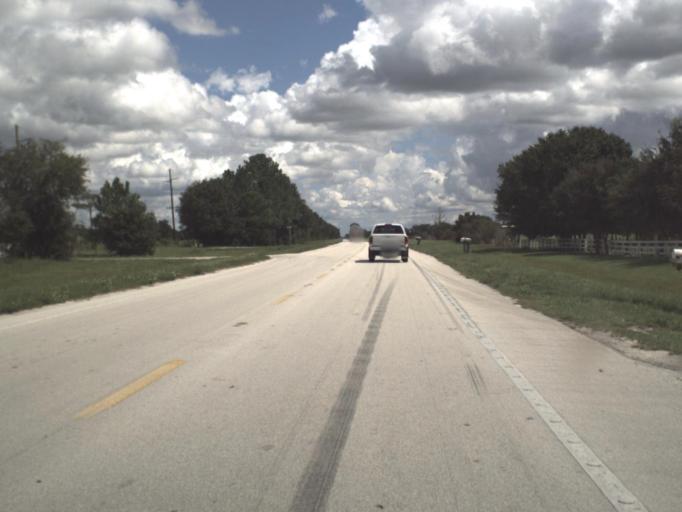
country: US
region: Florida
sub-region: DeSoto County
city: Southeast Arcadia
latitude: 27.2088
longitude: -81.7933
